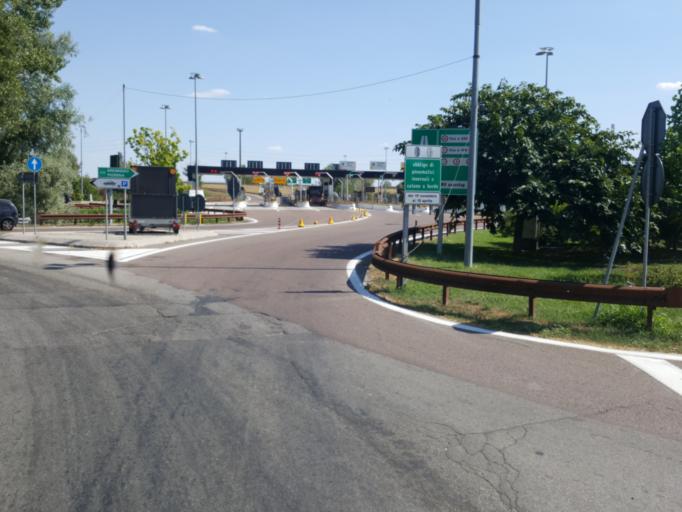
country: IT
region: Lombardy
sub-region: Provincia di Mantova
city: Bondeno
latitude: 44.9157
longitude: 10.8456
